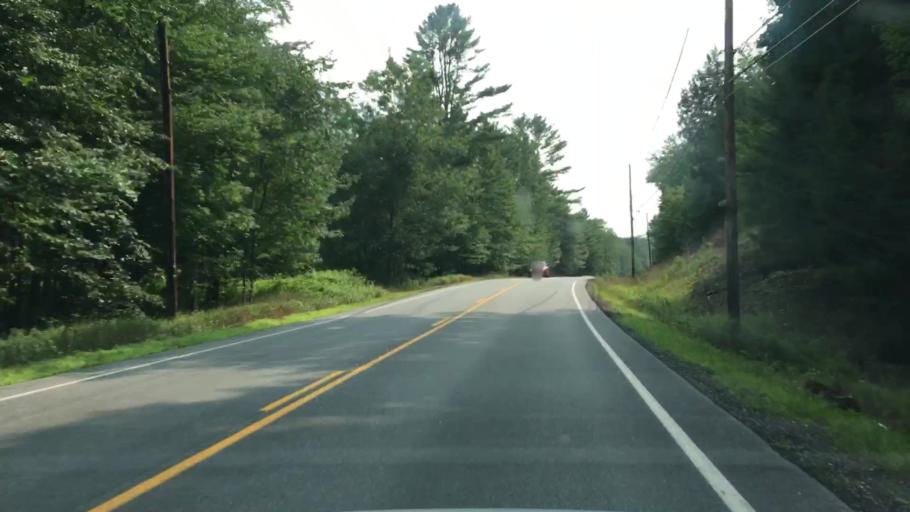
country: US
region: Maine
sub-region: Oxford County
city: South Paris
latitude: 44.2299
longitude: -70.4948
